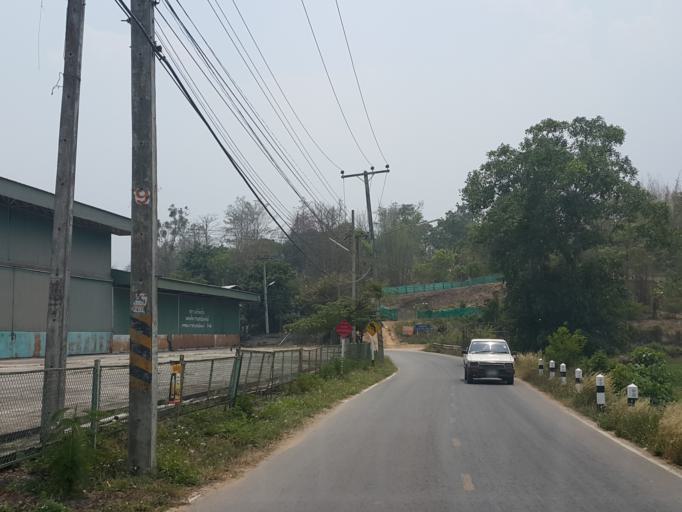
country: TH
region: Chiang Mai
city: Mae Taeng
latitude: 19.0405
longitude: 98.8698
